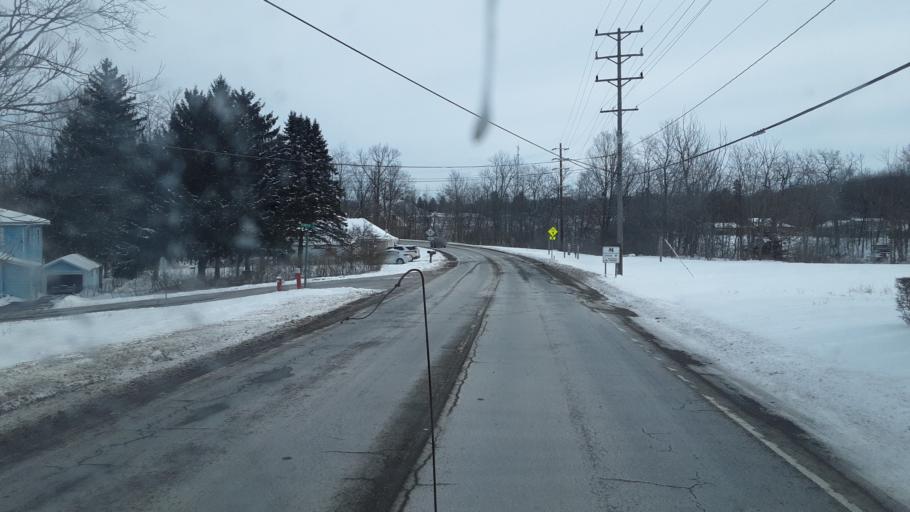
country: US
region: New York
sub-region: Wayne County
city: Newark
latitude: 43.0472
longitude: -77.0813
